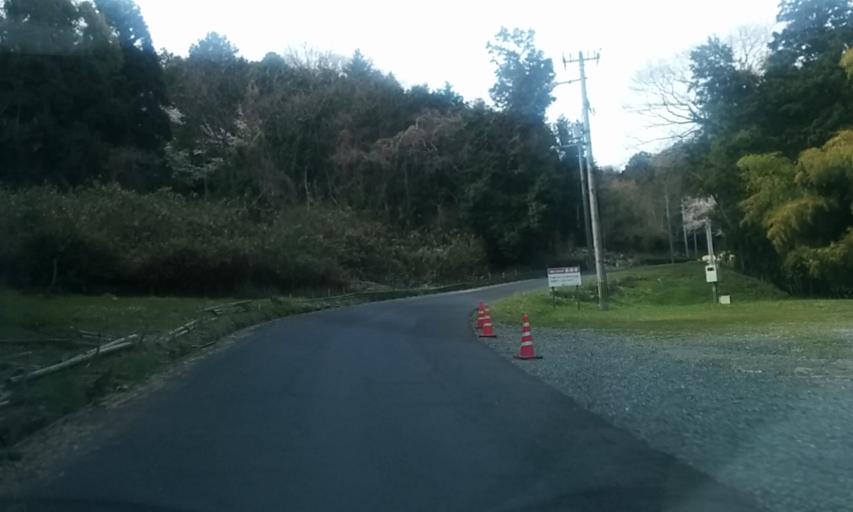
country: JP
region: Kyoto
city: Miyazu
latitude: 35.5816
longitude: 135.1774
